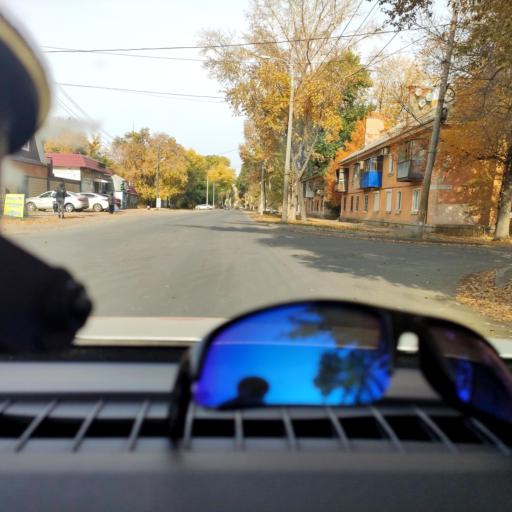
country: RU
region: Samara
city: Samara
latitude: 53.1115
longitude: 50.0754
